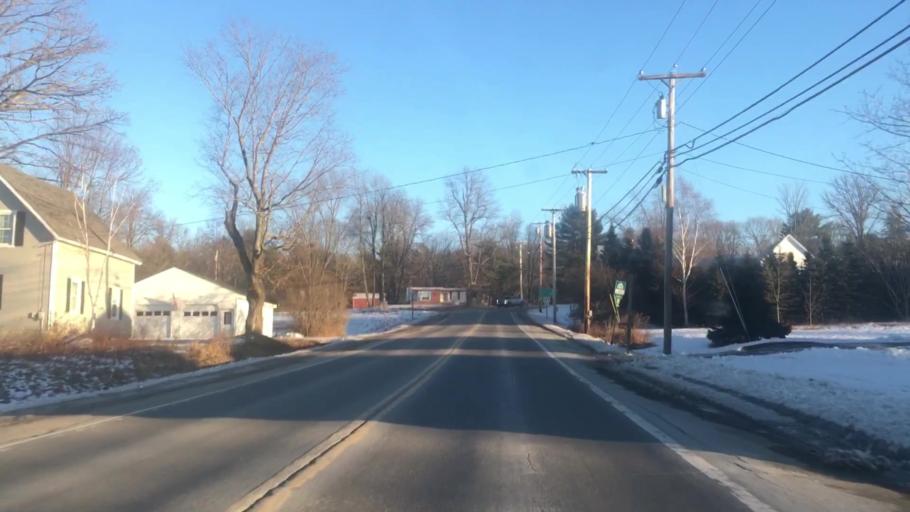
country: US
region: Maine
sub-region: Kennebec County
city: Benton
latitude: 44.5852
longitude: -69.5485
